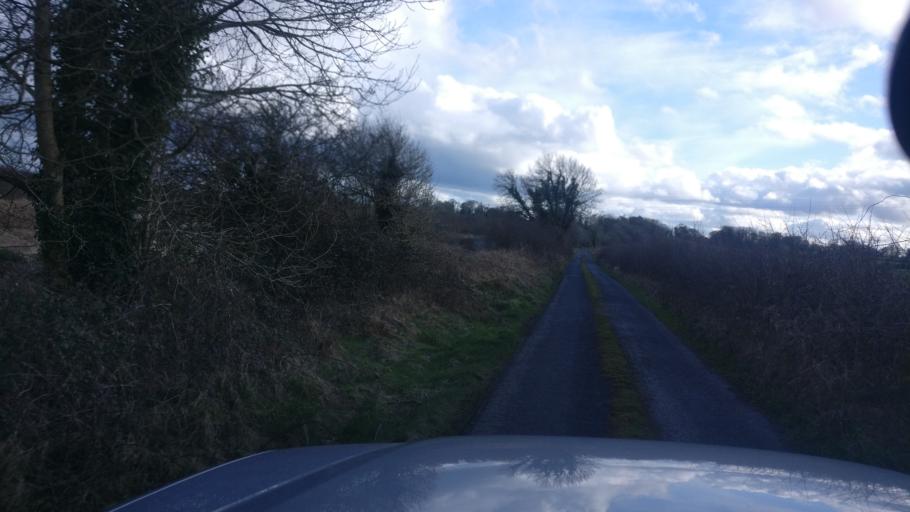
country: IE
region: Connaught
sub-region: County Galway
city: Loughrea
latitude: 53.1900
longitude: -8.4297
